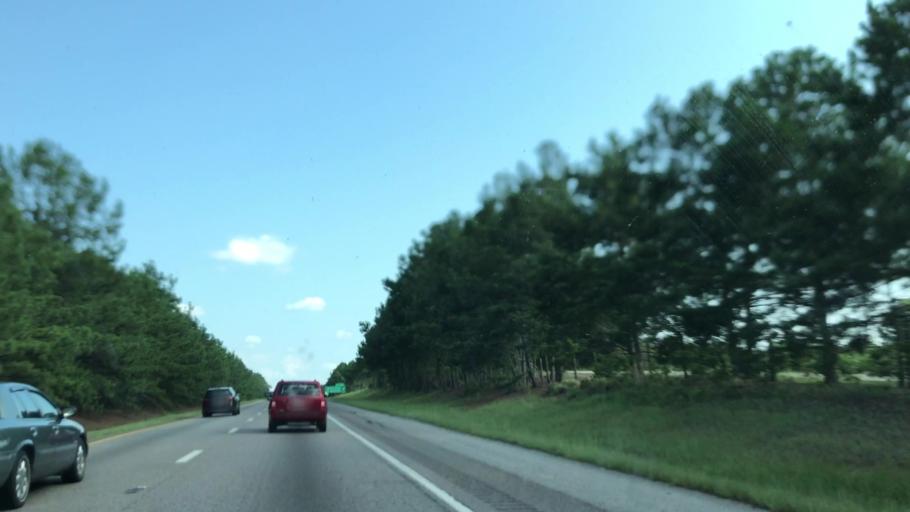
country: US
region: South Carolina
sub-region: Calhoun County
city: Saint Matthews
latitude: 33.6401
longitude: -80.8787
